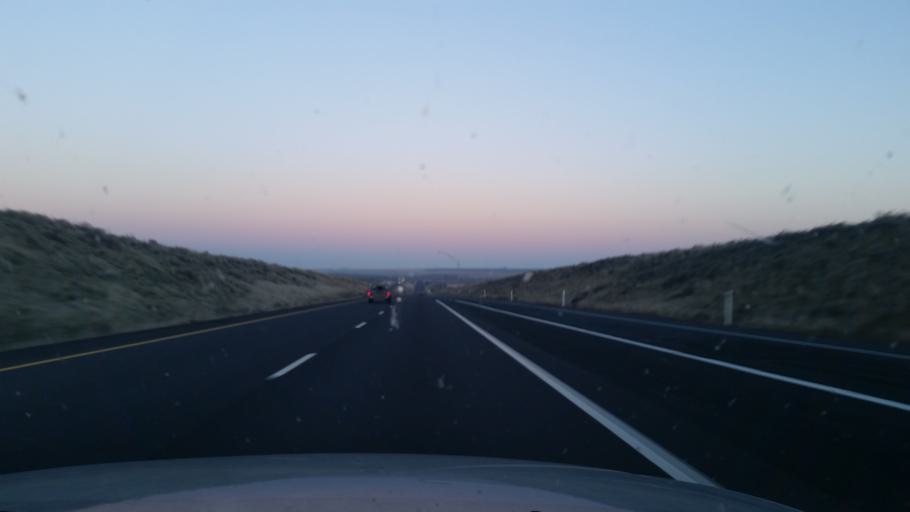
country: US
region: Washington
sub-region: Adams County
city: Ritzville
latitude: 47.0968
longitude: -118.6610
